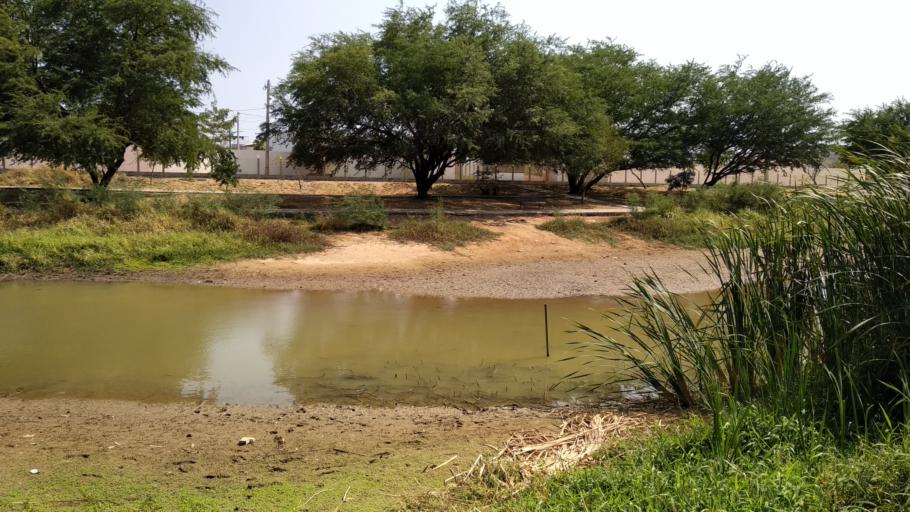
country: BR
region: Bahia
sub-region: Guanambi
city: Guanambi
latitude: -14.2247
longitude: -42.7644
